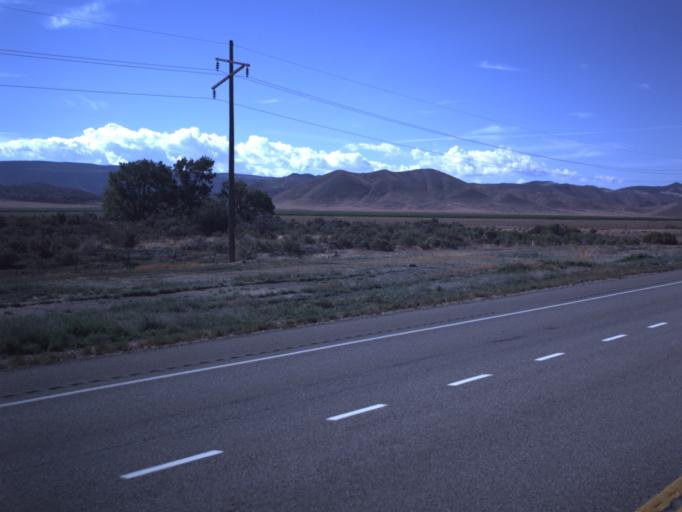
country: US
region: Utah
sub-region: Sanpete County
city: Centerfield
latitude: 39.0467
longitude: -111.8248
